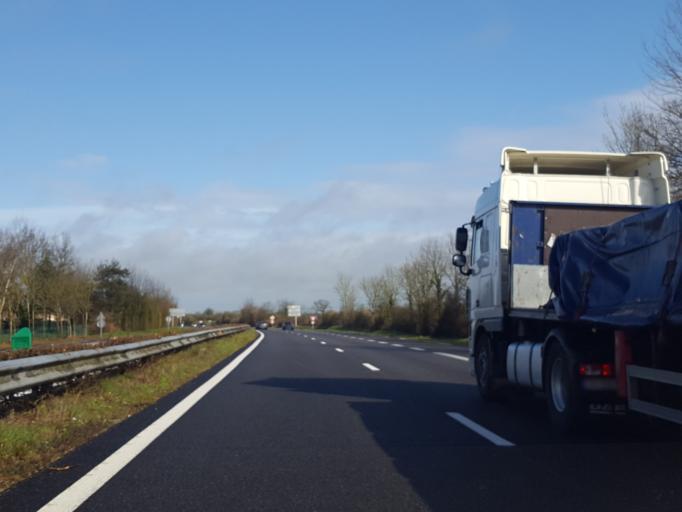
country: FR
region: Pays de la Loire
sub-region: Departement de la Vendee
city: Belleville-sur-Vie
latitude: 46.7831
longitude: -1.4204
